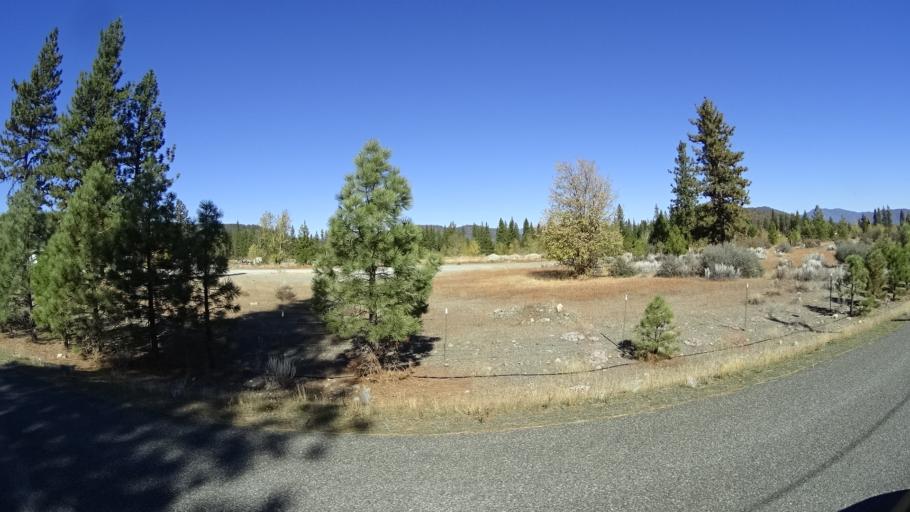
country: US
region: California
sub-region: Siskiyou County
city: Yreka
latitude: 41.5387
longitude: -122.9177
